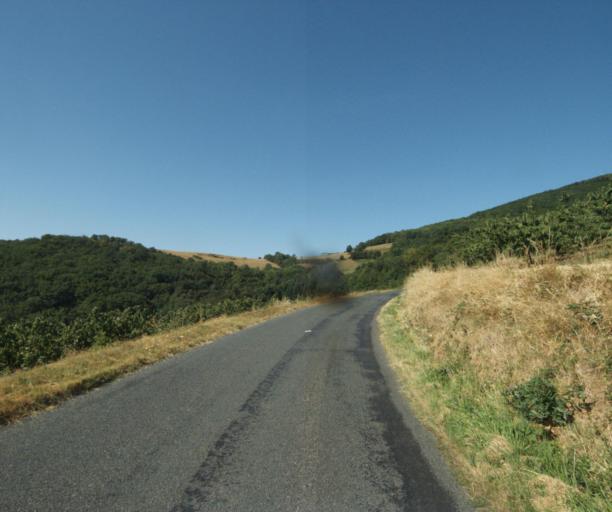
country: FR
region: Rhone-Alpes
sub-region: Departement du Rhone
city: Saint-Romain-de-Popey
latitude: 45.8208
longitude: 4.5329
